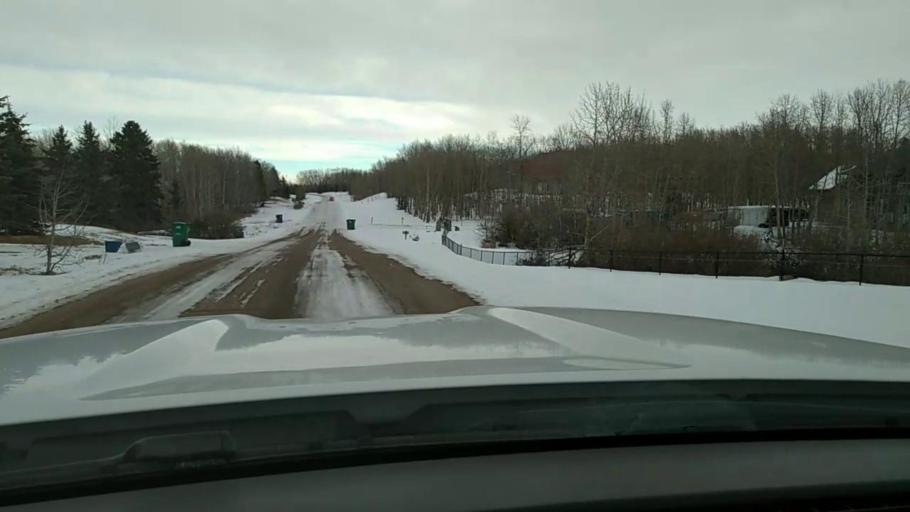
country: CA
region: Alberta
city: Calgary
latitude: 51.1804
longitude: -114.2544
